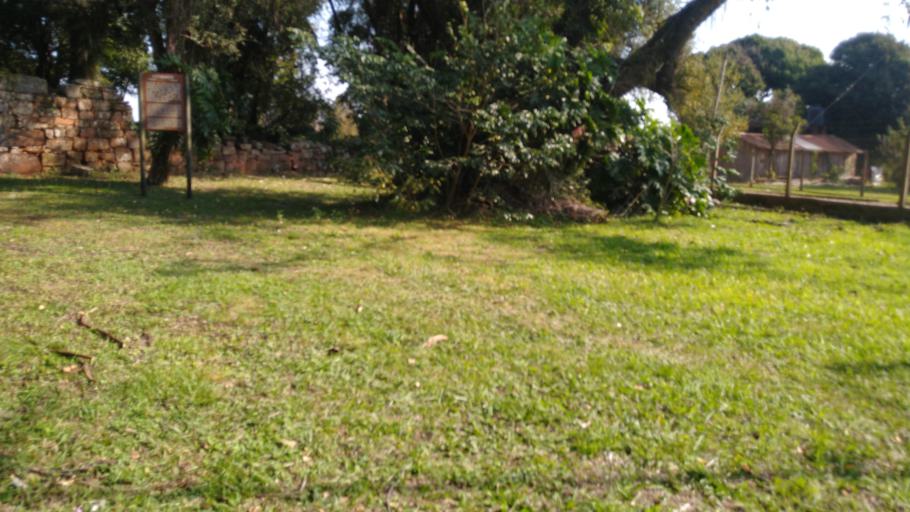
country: AR
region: Misiones
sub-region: Departamento de San Ignacio
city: San Ignacio
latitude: -27.2552
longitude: -55.5326
